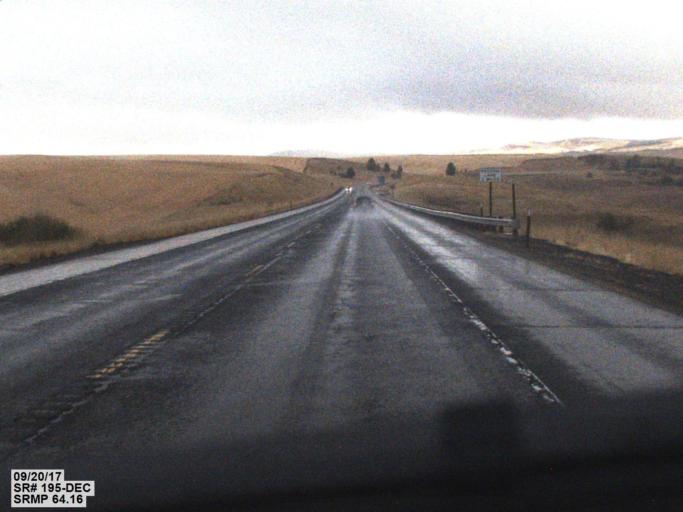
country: US
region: Washington
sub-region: Spokane County
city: Cheney
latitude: 47.2310
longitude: -117.3574
